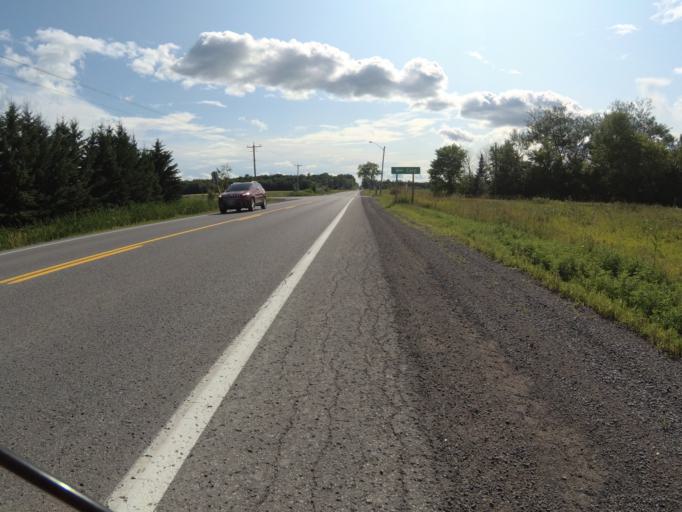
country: CA
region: Ontario
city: Arnprior
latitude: 45.4645
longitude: -76.1906
